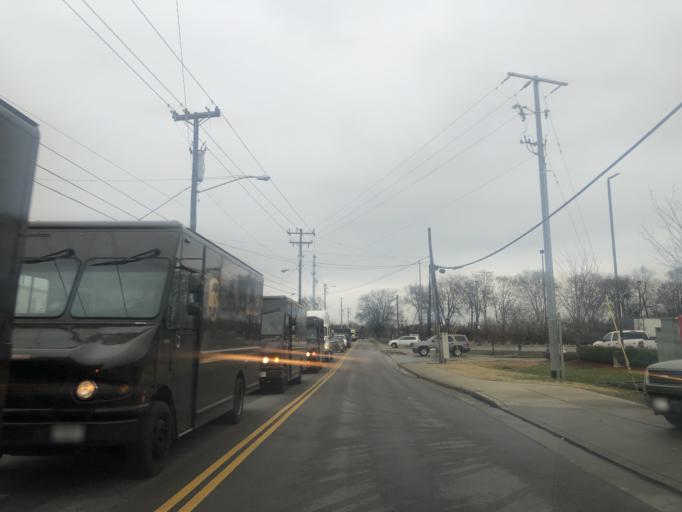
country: US
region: Tennessee
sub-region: Davidson County
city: Nashville
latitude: 36.1395
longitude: -86.7327
